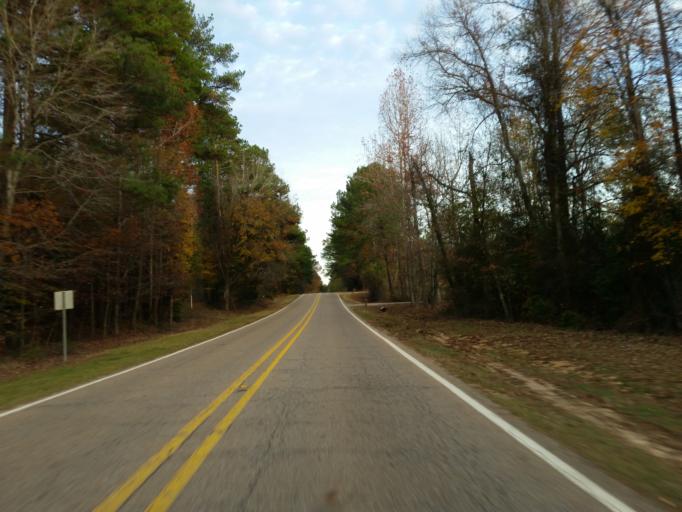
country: US
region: Alabama
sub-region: Sumter County
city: York
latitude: 32.4241
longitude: -88.4182
